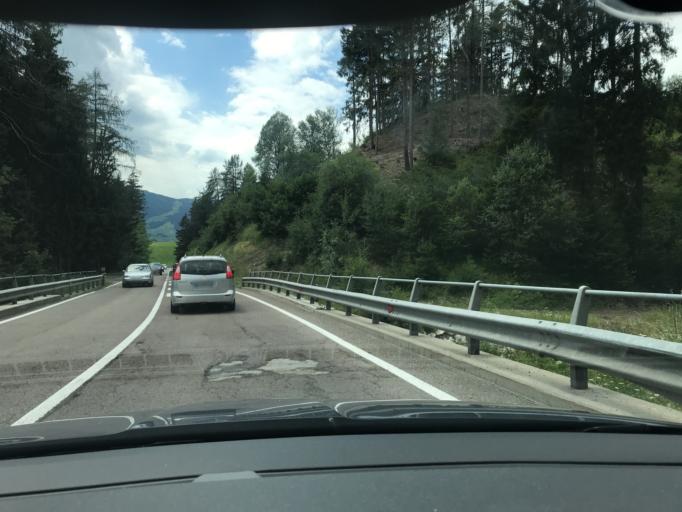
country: IT
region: Trentino-Alto Adige
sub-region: Bolzano
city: Monguelfo
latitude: 46.7631
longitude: 12.0807
